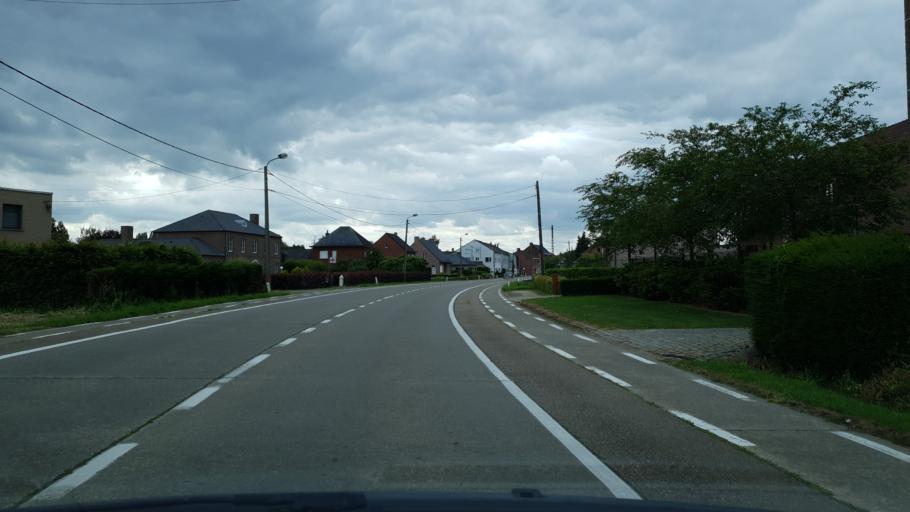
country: BE
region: Flanders
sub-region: Provincie Antwerpen
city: Hulshout
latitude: 51.0525
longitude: 4.7907
